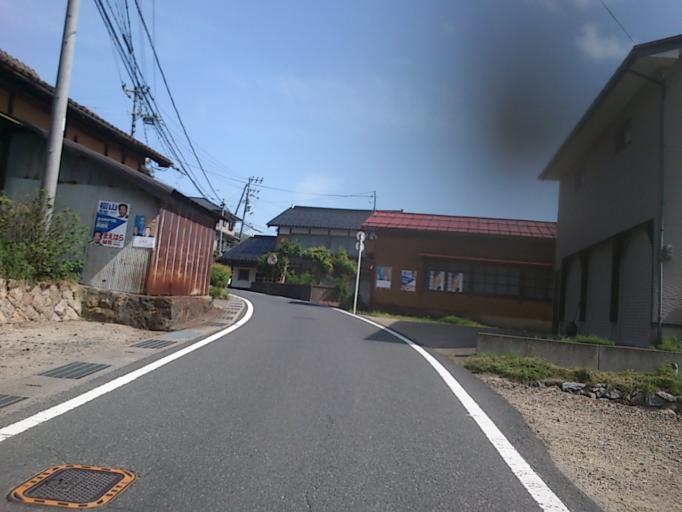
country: JP
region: Kyoto
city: Miyazu
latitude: 35.5697
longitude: 135.1161
